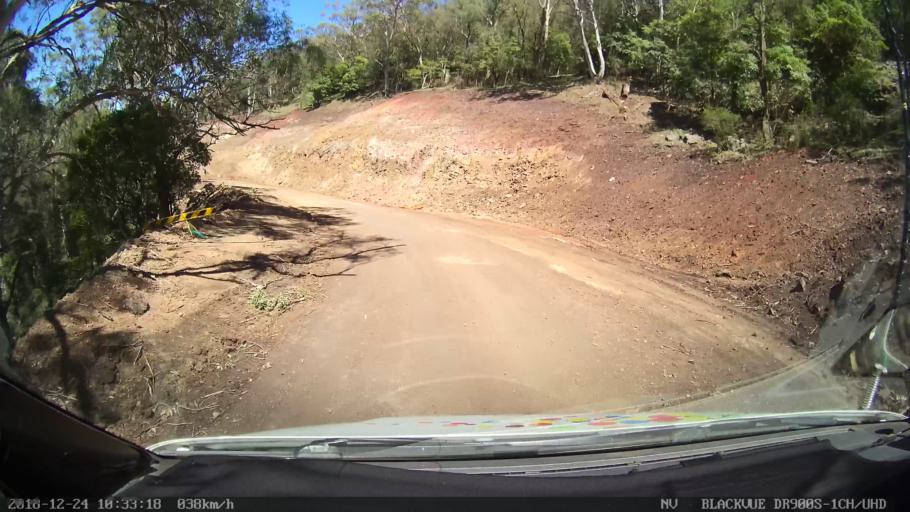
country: AU
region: New South Wales
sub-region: Upper Hunter Shire
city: Merriwa
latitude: -31.8411
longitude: 150.5111
